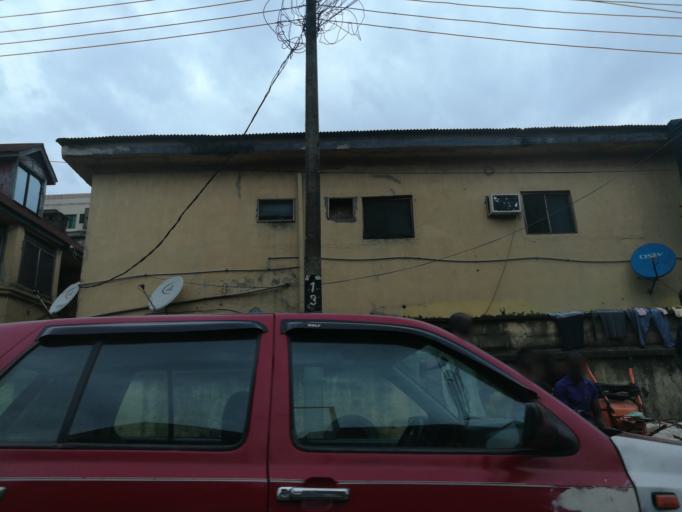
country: NG
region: Lagos
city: Ebute Metta
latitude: 6.4840
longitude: 3.3832
